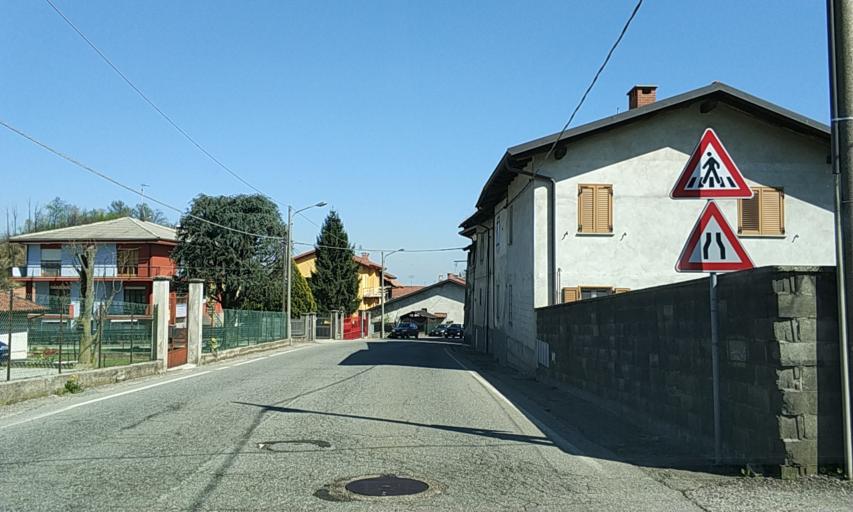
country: IT
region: Piedmont
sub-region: Provincia di Torino
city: Forno Canavese
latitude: 45.3382
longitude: 7.6015
